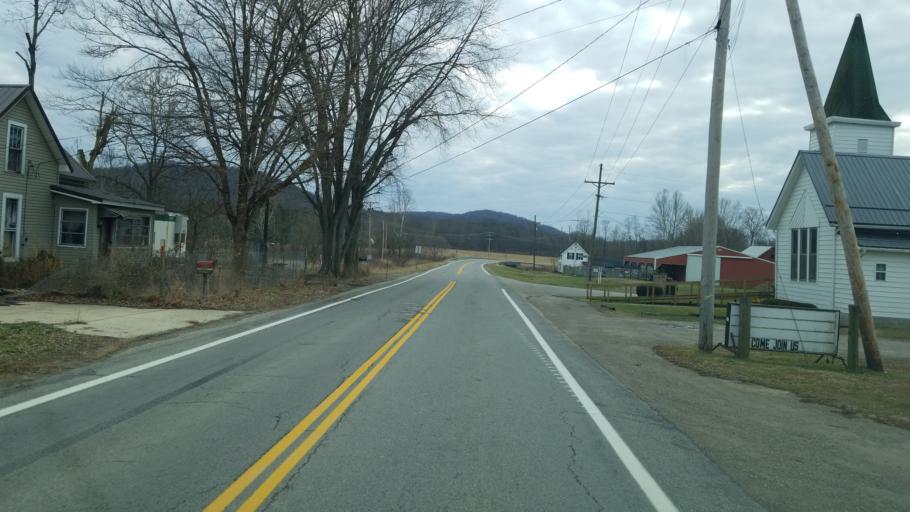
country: US
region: Ohio
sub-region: Highland County
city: Greenfield
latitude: 39.3022
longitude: -83.3398
